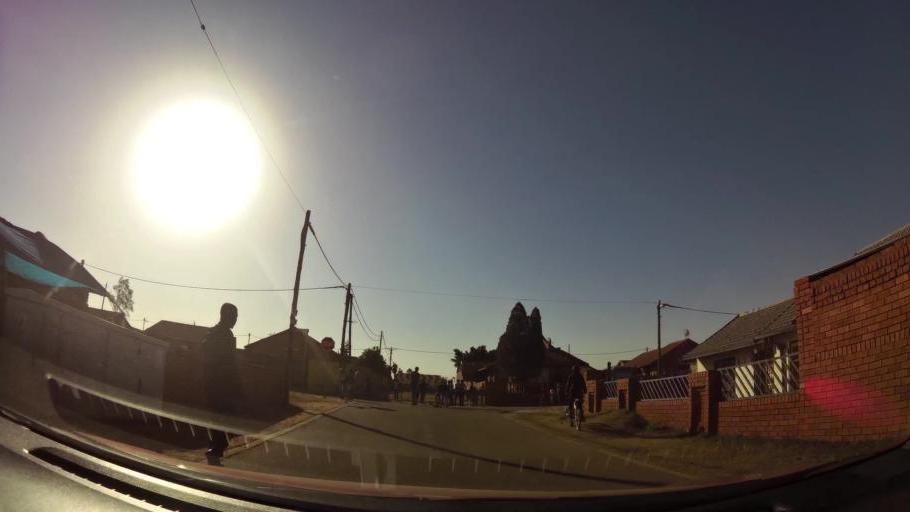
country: ZA
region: Gauteng
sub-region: City of Tshwane Metropolitan Municipality
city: Mabopane
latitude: -25.5842
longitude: 28.1081
